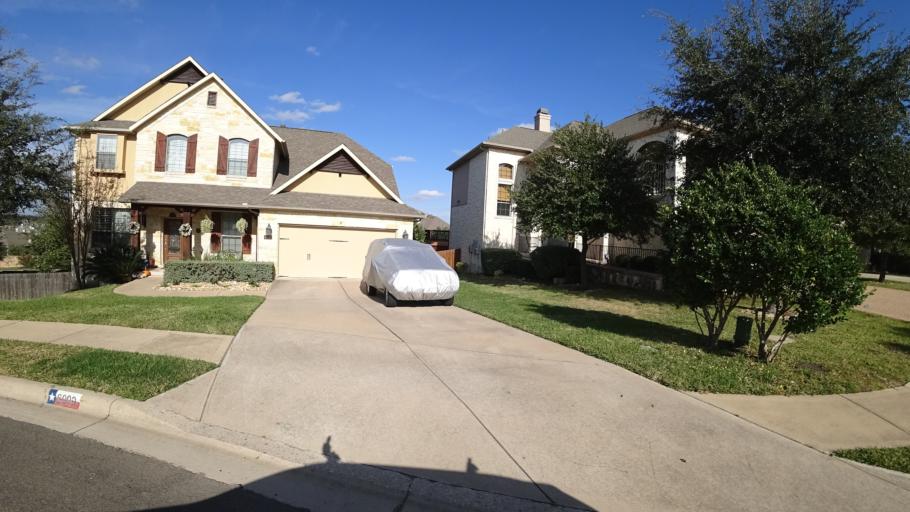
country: US
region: Texas
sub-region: Travis County
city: Barton Creek
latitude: 30.2484
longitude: -97.8767
